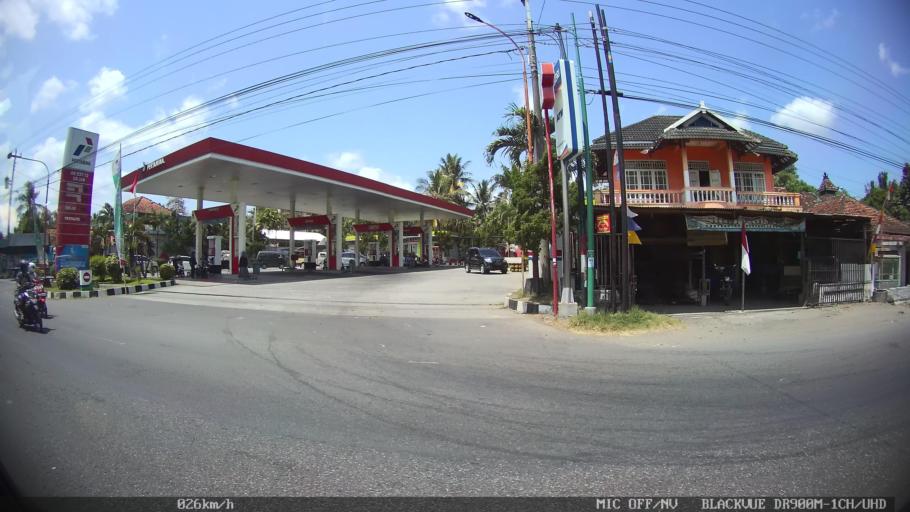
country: ID
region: Daerah Istimewa Yogyakarta
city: Pandak
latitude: -7.9109
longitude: 110.2934
